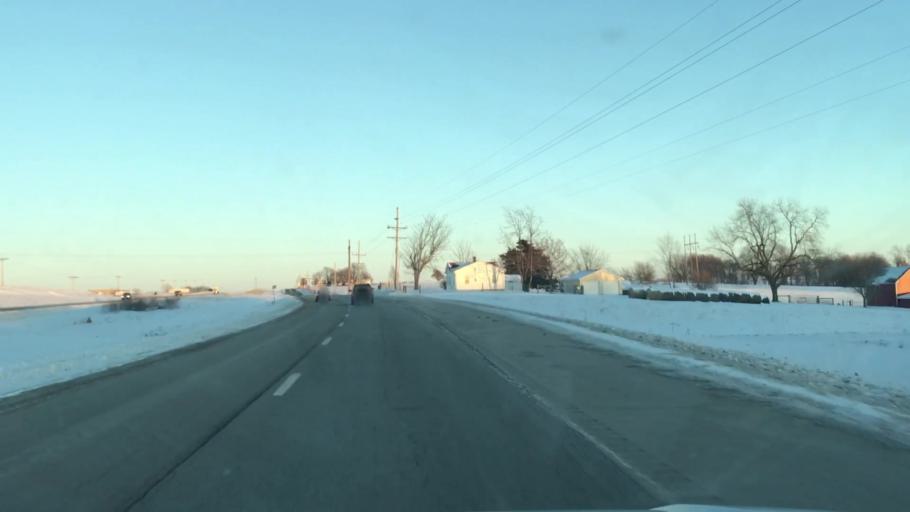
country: US
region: Missouri
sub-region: Clinton County
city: Cameron
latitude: 39.7547
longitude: -94.3109
